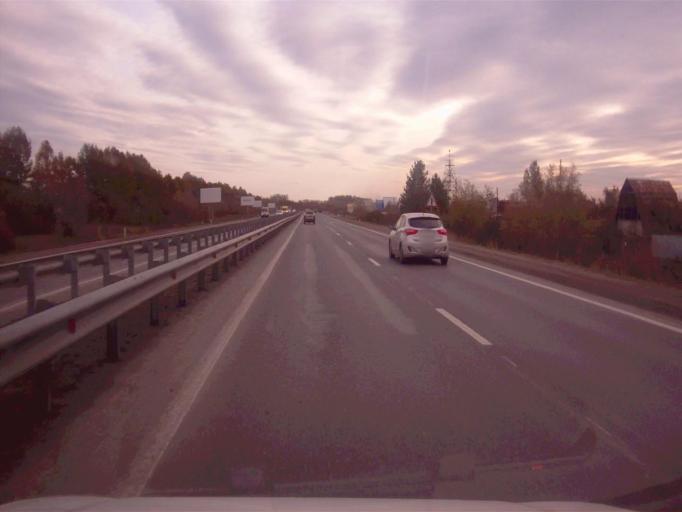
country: RU
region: Chelyabinsk
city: Novosineglazovskiy
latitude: 55.0253
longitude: 61.4506
